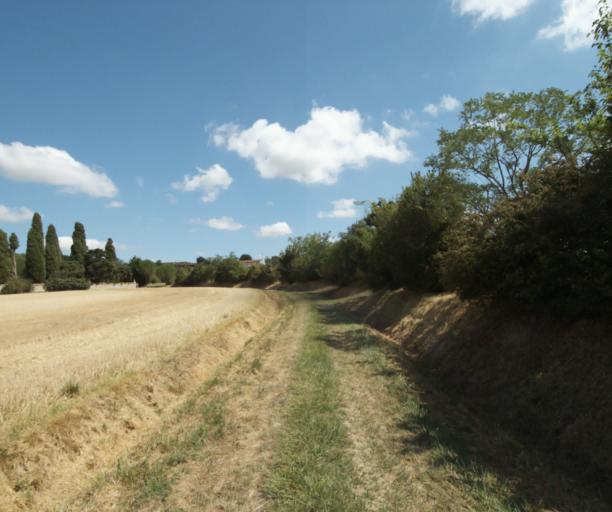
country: FR
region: Midi-Pyrenees
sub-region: Departement de la Haute-Garonne
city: Auriac-sur-Vendinelle
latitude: 43.4624
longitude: 1.7947
